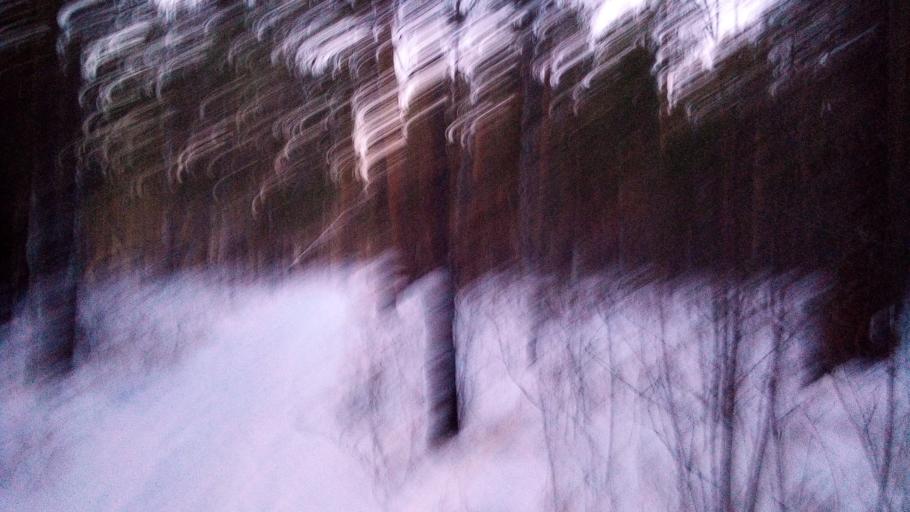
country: RU
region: Chelyabinsk
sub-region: Gorod Chelyabinsk
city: Chelyabinsk
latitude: 55.1640
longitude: 61.3318
